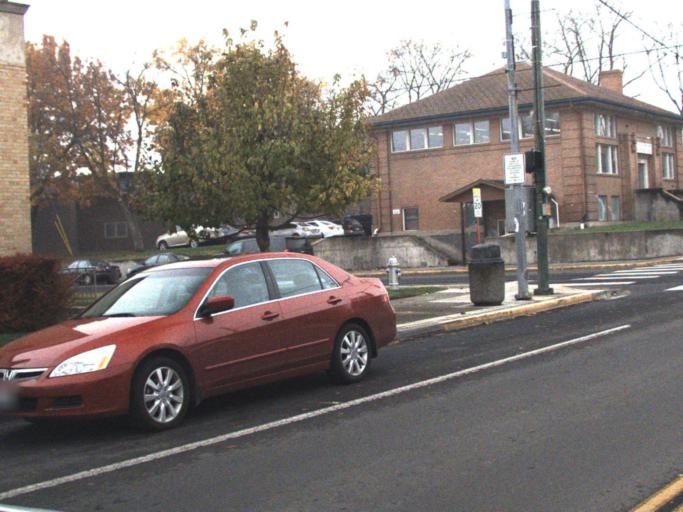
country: US
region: Washington
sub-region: Asotin County
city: Clarkston
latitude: 46.4111
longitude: -117.0455
